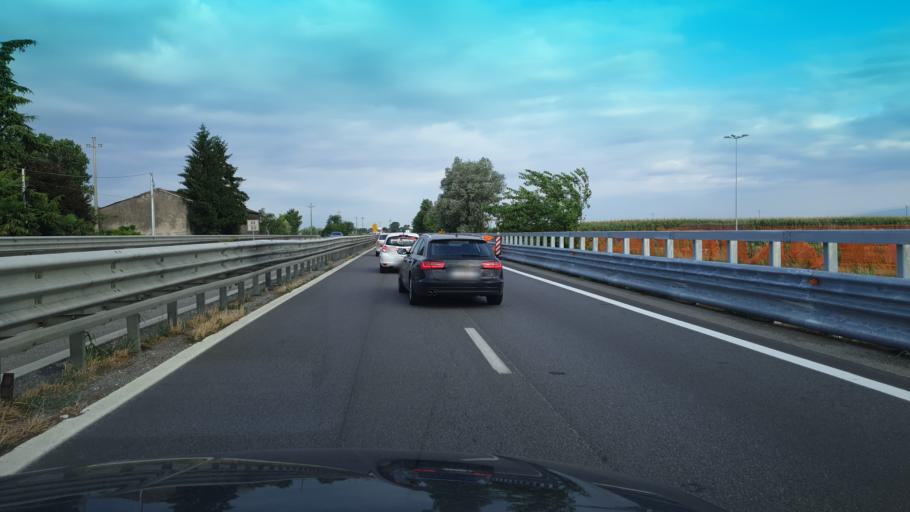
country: IT
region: Veneto
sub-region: Provincia di Verona
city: Oppeano
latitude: 45.2970
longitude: 11.1586
